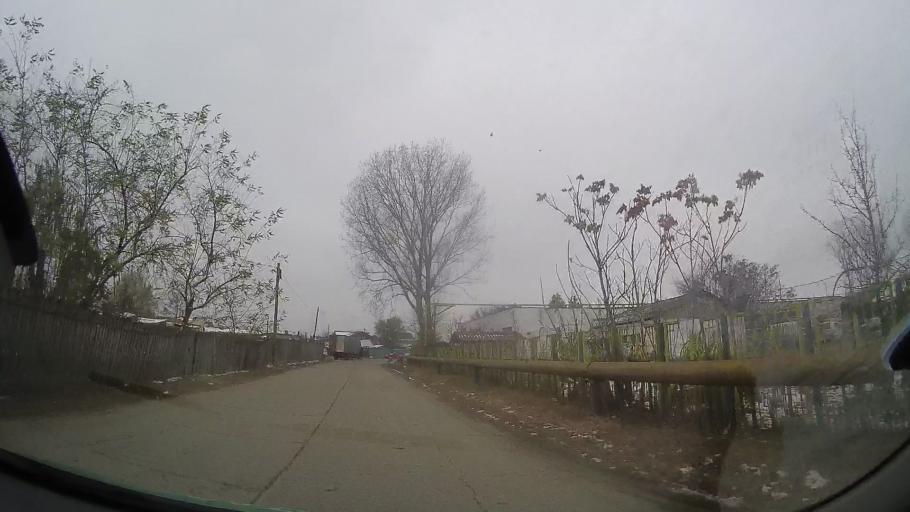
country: RO
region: Vaslui
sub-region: Municipiul Barlad
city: Barlad
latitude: 46.2379
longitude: 27.6808
